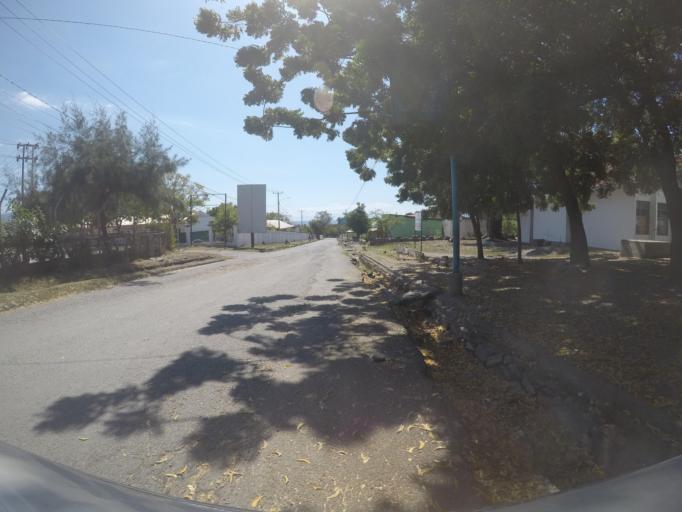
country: TL
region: Liquica
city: Liquica
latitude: -8.5943
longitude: 125.3289
